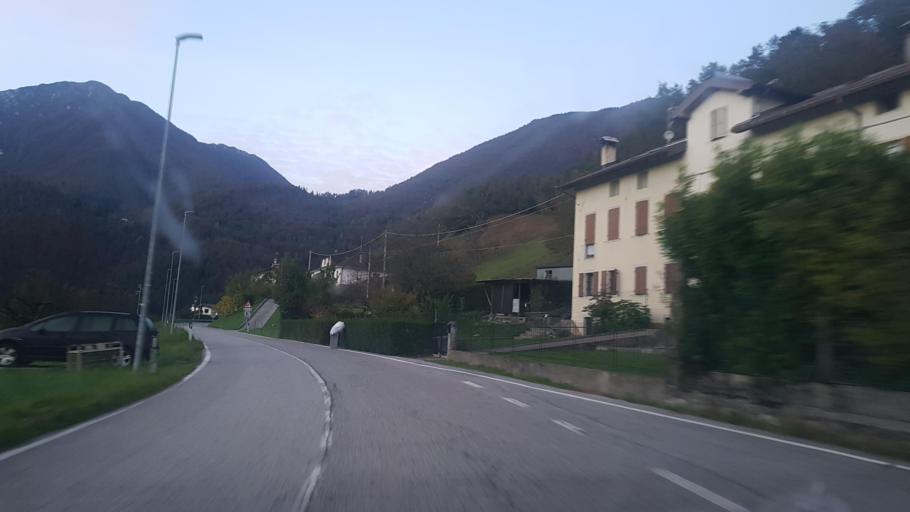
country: IT
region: Friuli Venezia Giulia
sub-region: Provincia di Udine
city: Chiaulis
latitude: 46.3835
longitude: 12.9740
